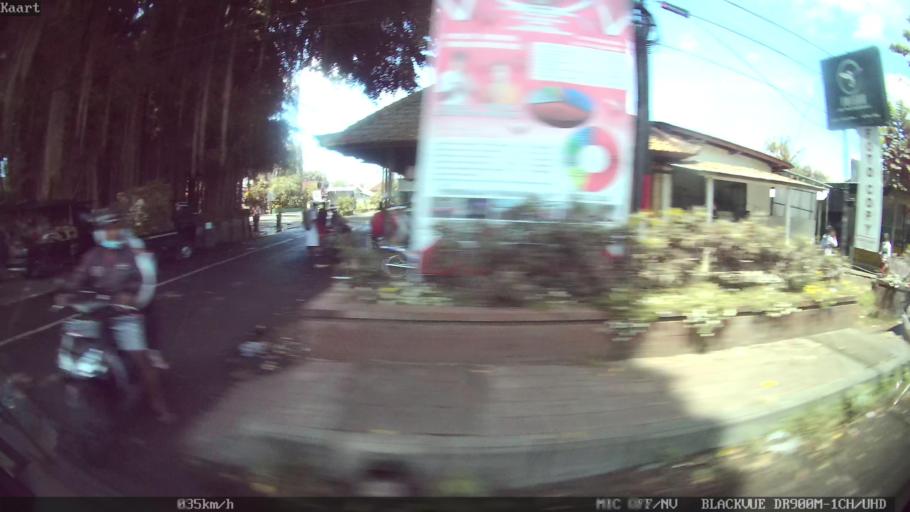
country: ID
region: Bali
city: Banjar Jabejero
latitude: -8.5927
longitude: 115.2562
